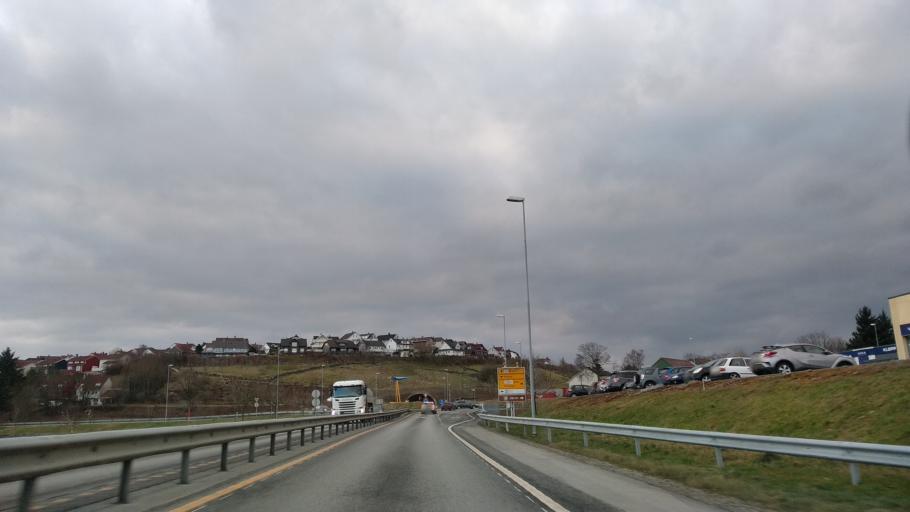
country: NO
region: Rogaland
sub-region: Klepp
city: Kleppe
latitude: 58.7799
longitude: 5.6249
